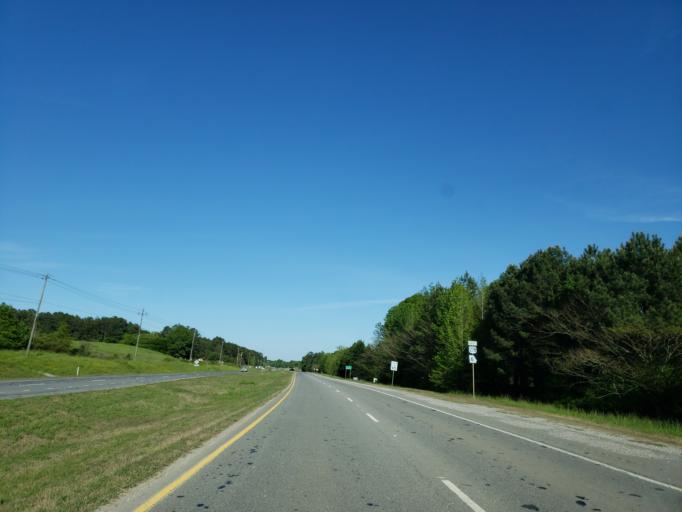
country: US
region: Georgia
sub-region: Polk County
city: Cedartown
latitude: 34.0037
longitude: -85.1669
